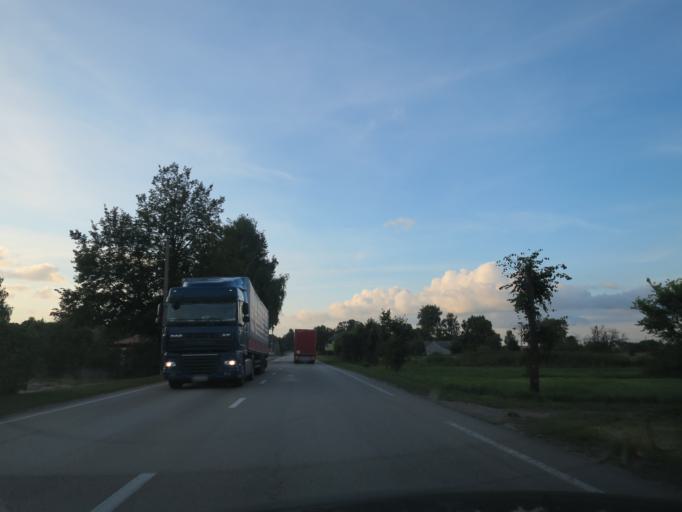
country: LV
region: Salacgrivas
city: Salacgriva
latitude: 57.7587
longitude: 24.3603
